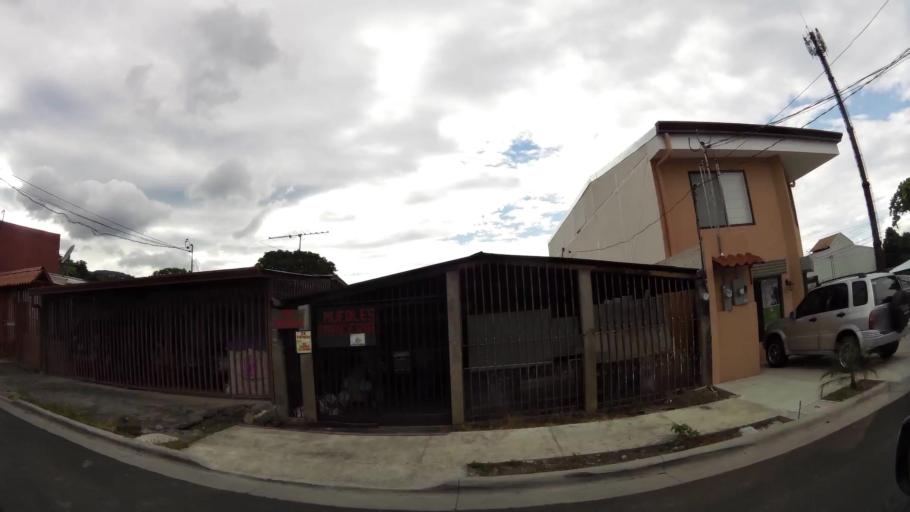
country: CR
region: San Jose
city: Santa Ana
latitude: 9.9322
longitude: -84.1838
